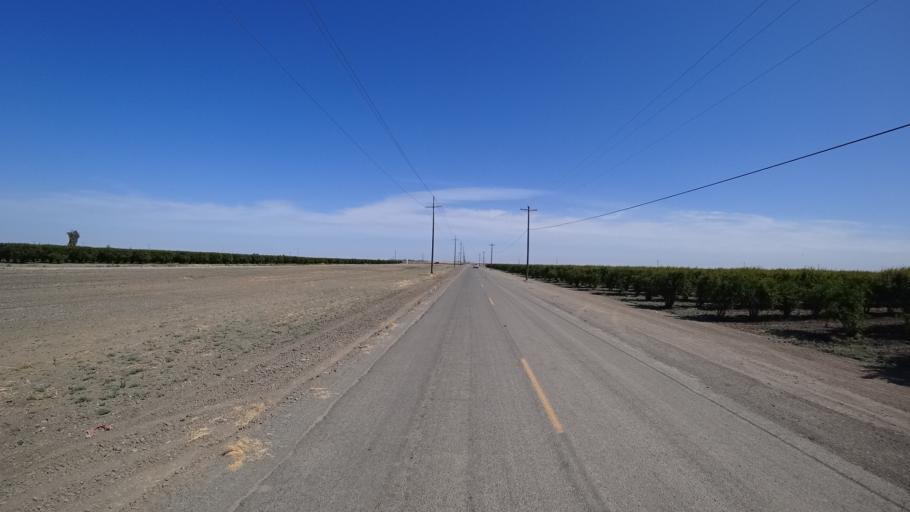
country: US
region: California
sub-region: Kings County
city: Stratford
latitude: 36.2521
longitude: -119.8344
